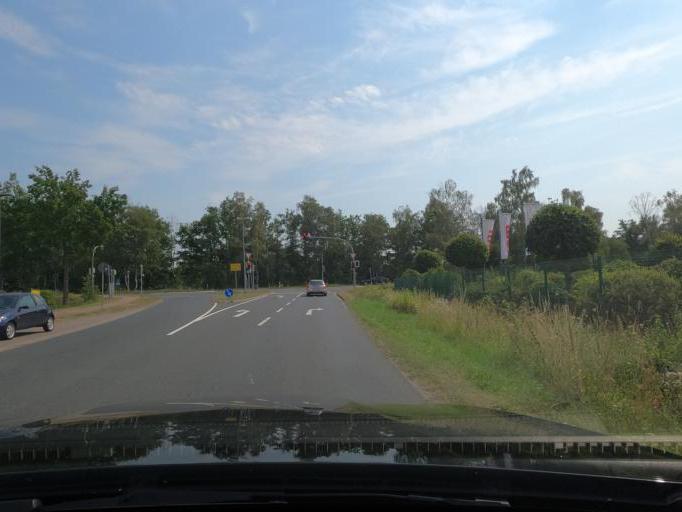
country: DE
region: Lower Saxony
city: Isernhagen Farster Bauerschaft
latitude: 52.4375
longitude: 9.8844
